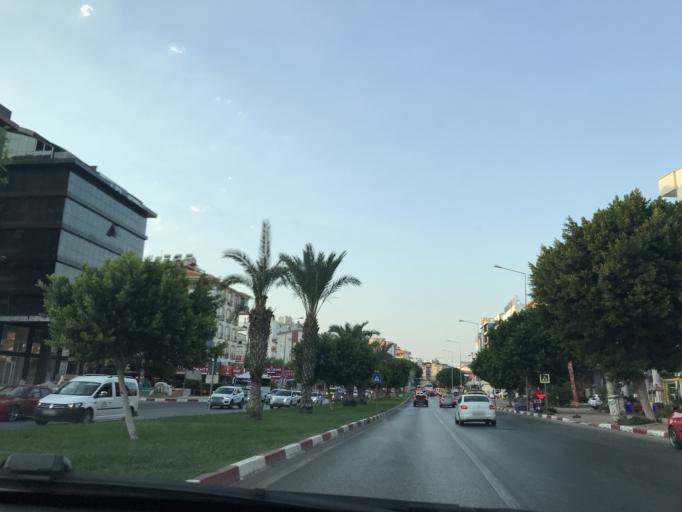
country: TR
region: Antalya
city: Antalya
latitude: 36.8723
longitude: 30.6417
